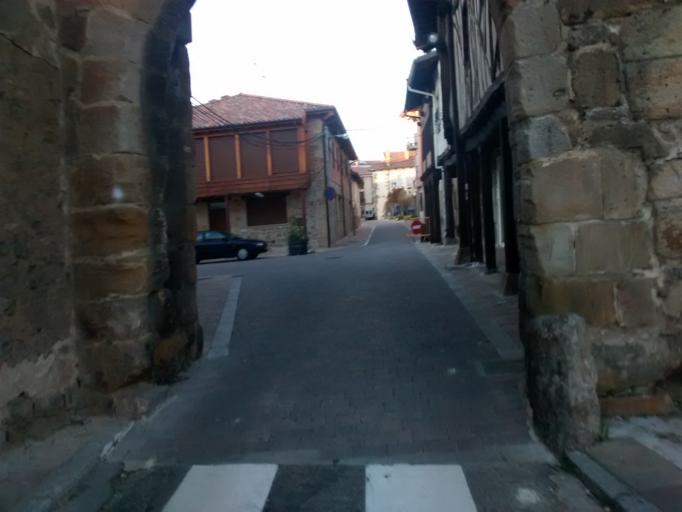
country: ES
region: Castille and Leon
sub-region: Provincia de Palencia
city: Aguilar de Campoo
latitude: 42.7921
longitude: -4.2574
